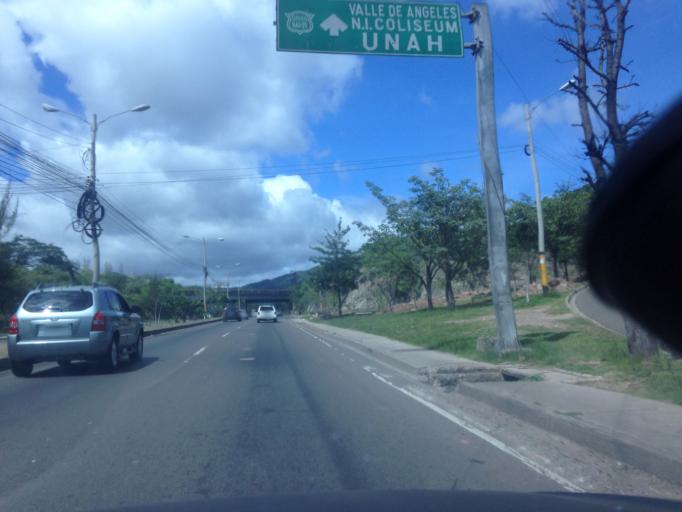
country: HN
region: Francisco Morazan
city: Tegucigalpa
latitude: 14.0811
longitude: -87.1627
